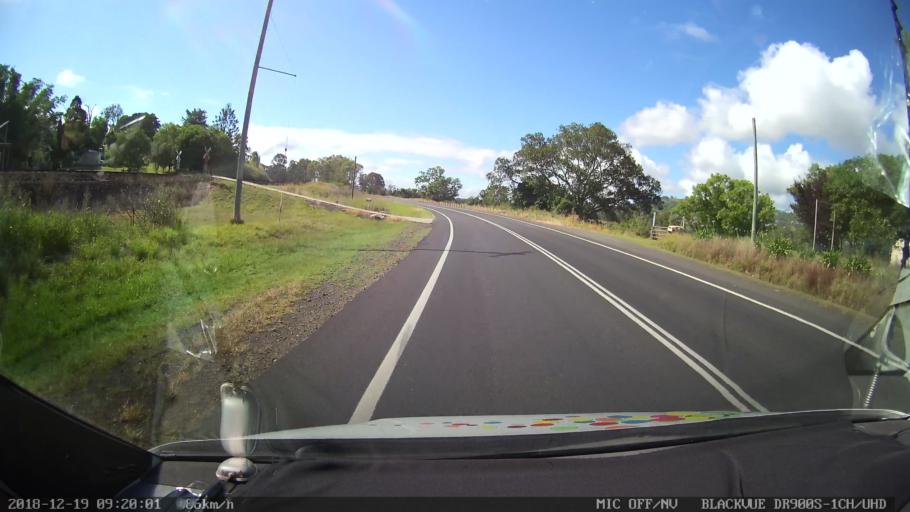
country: AU
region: New South Wales
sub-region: Kyogle
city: Kyogle
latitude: -28.5674
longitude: 152.9777
